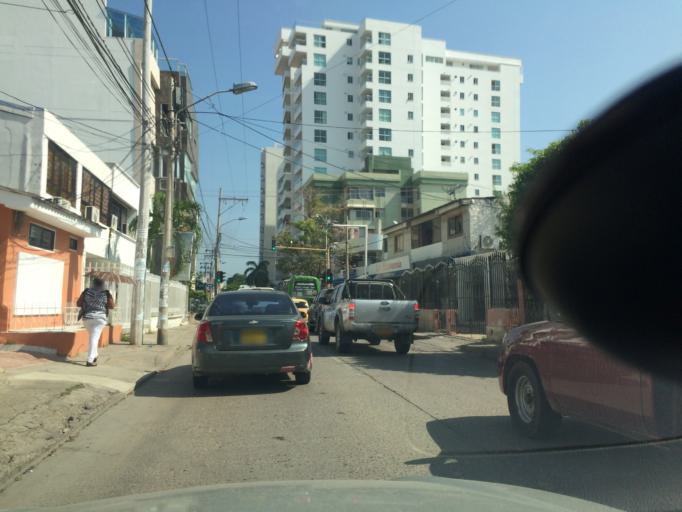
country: CO
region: Bolivar
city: Cartagena
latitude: 10.4129
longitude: -75.5336
